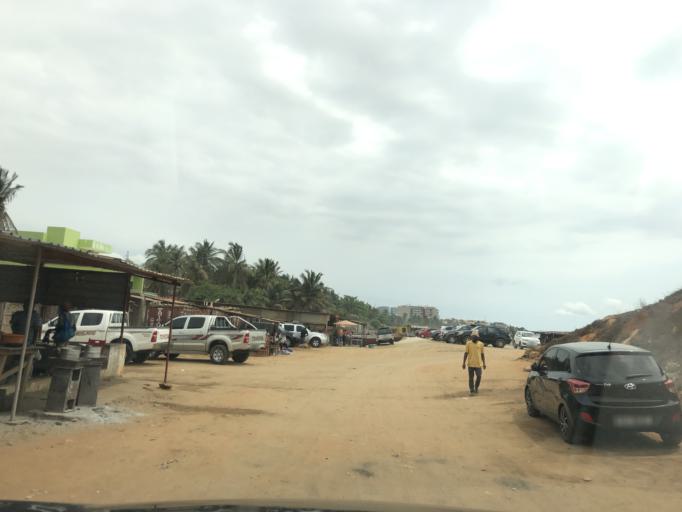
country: AO
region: Luanda
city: Luanda
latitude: -8.8713
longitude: 13.1948
